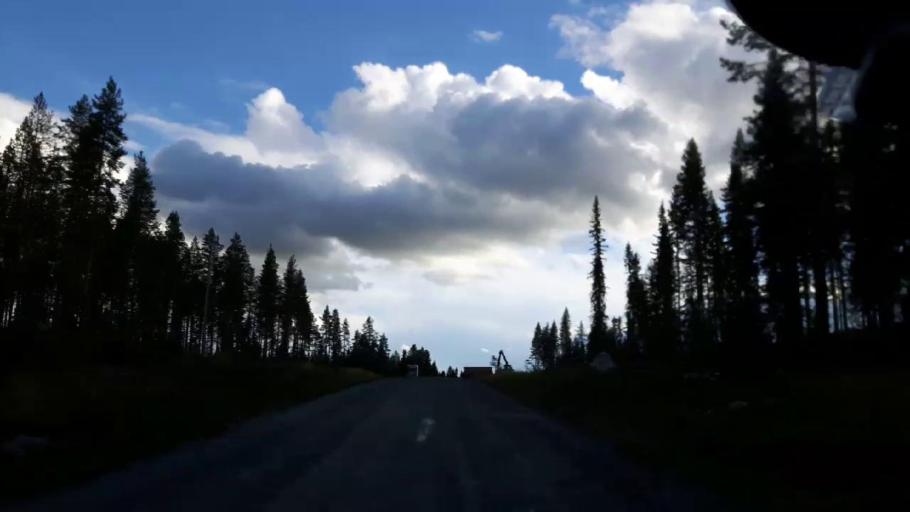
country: SE
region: Jaemtland
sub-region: Stroemsunds Kommun
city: Stroemsund
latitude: 63.3383
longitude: 15.5656
